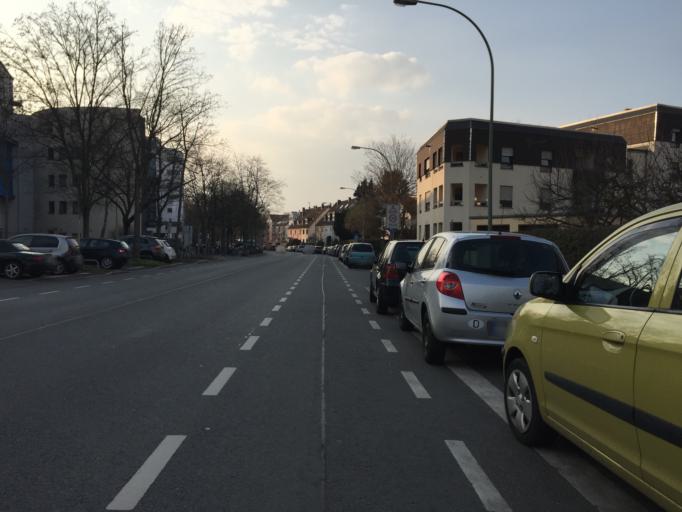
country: DE
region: Hesse
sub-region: Regierungsbezirk Darmstadt
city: Frankfurt am Main
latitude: 50.1367
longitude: 8.6488
